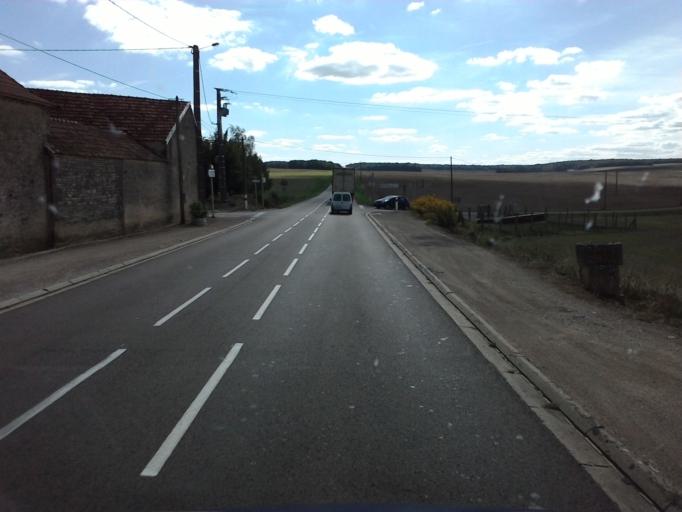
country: FR
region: Bourgogne
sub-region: Departement de la Cote-d'Or
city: Chatillon-sur-Seine
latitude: 47.8080
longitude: 4.5280
